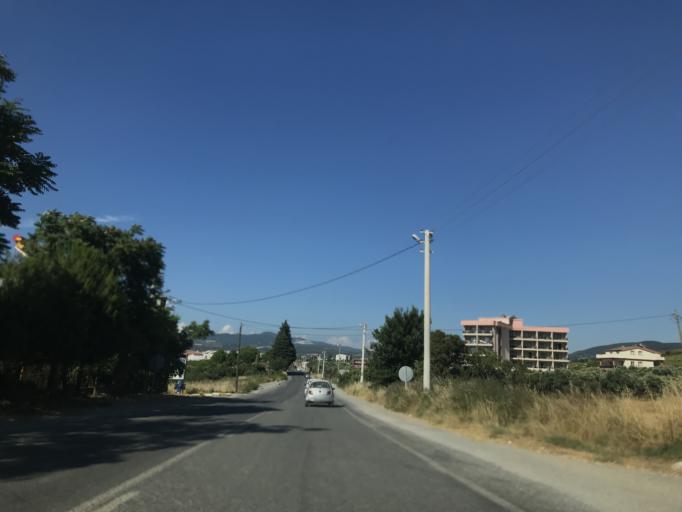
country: TR
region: Aydin
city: Davutlar
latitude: 37.7286
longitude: 27.2671
